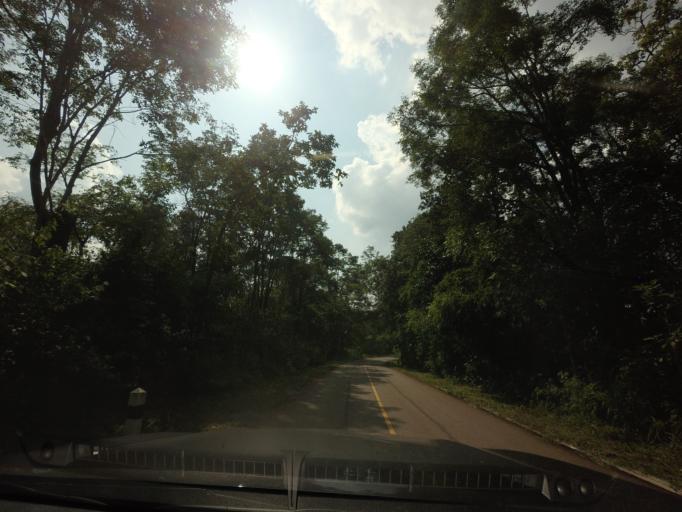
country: TH
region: Uttaradit
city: Ban Khok
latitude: 18.1798
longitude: 101.0692
